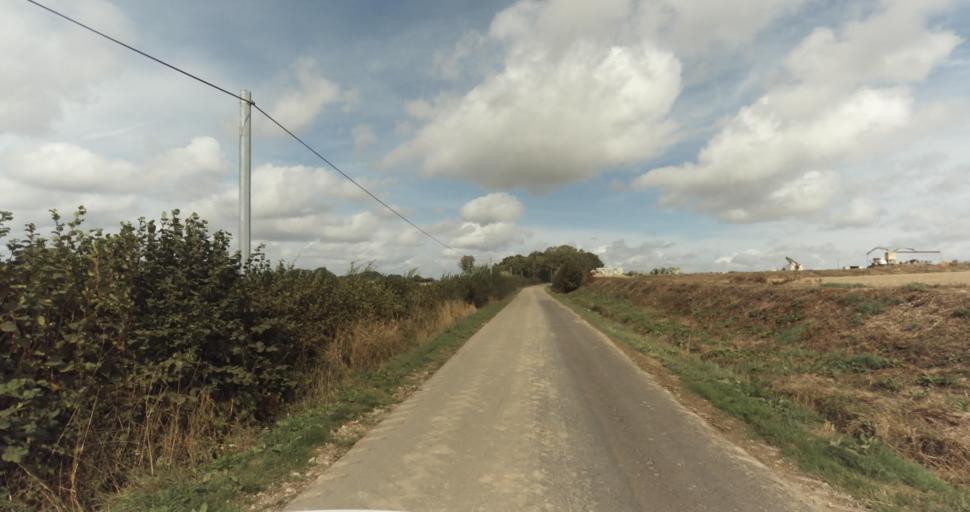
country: FR
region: Lower Normandy
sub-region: Departement de l'Orne
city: Gace
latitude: 48.8051
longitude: 0.3880
